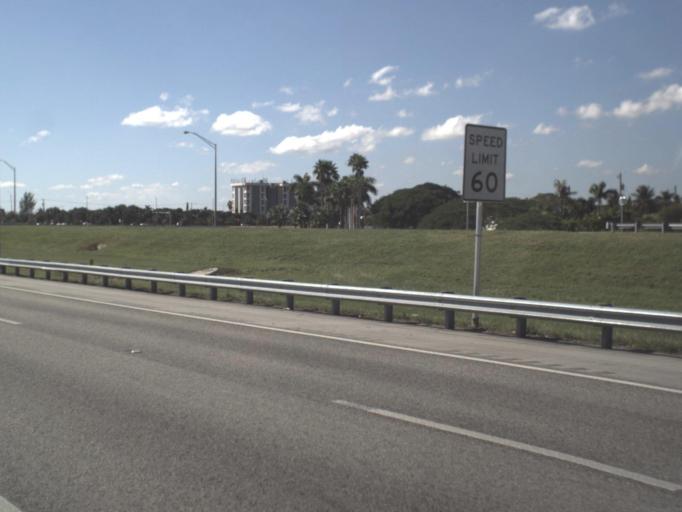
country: US
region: Florida
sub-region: Miami-Dade County
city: Sweetwater
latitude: 25.7652
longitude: -80.3857
